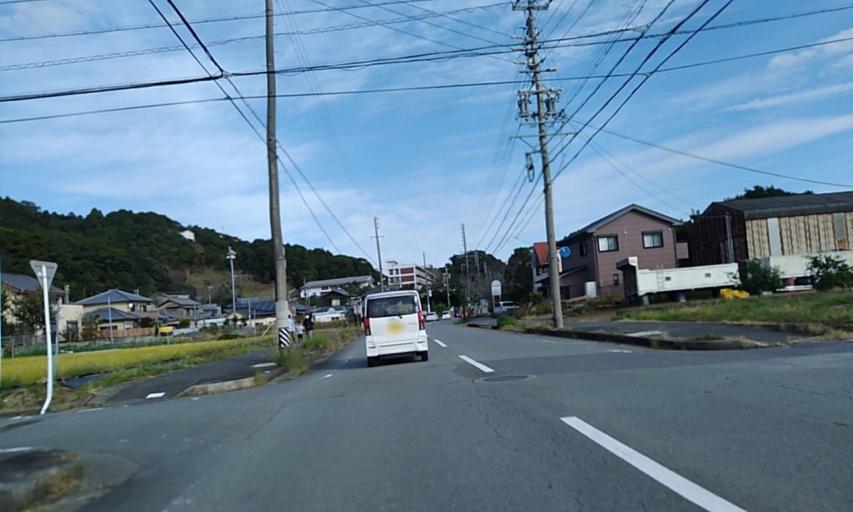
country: JP
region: Mie
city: Ise
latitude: 34.3495
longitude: 136.7051
